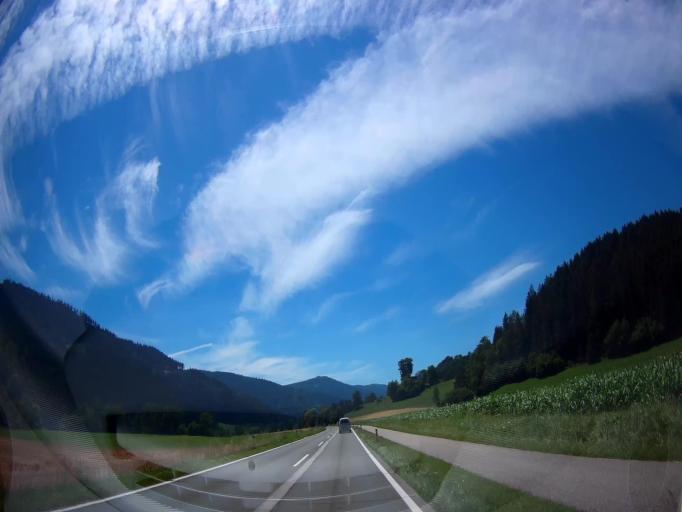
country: AT
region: Carinthia
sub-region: Politischer Bezirk Sankt Veit an der Glan
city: Strassburg
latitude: 46.8882
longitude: 14.3166
